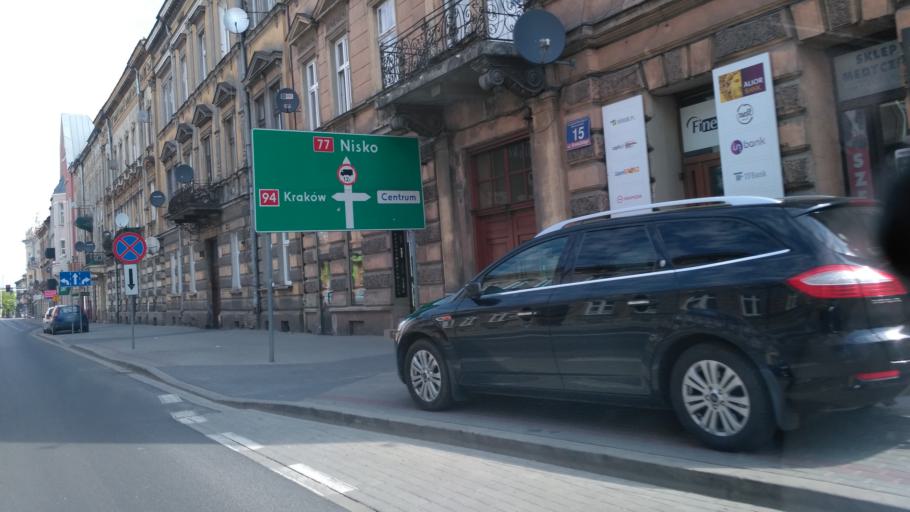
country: PL
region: Subcarpathian Voivodeship
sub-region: Powiat jaroslawski
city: Jaroslaw
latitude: 50.0144
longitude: 22.6781
